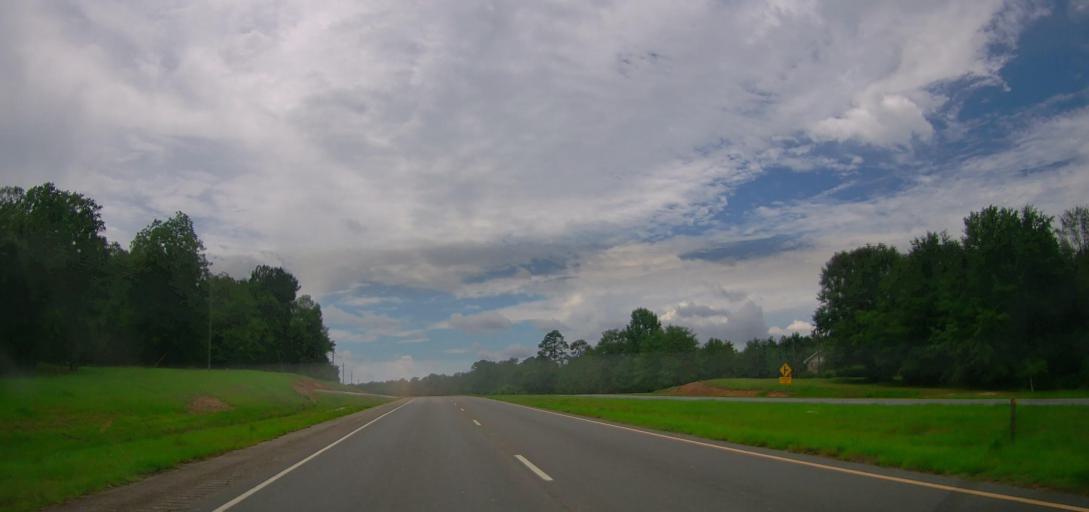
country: US
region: Georgia
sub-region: Telfair County
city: Helena
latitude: 32.1050
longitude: -82.9740
